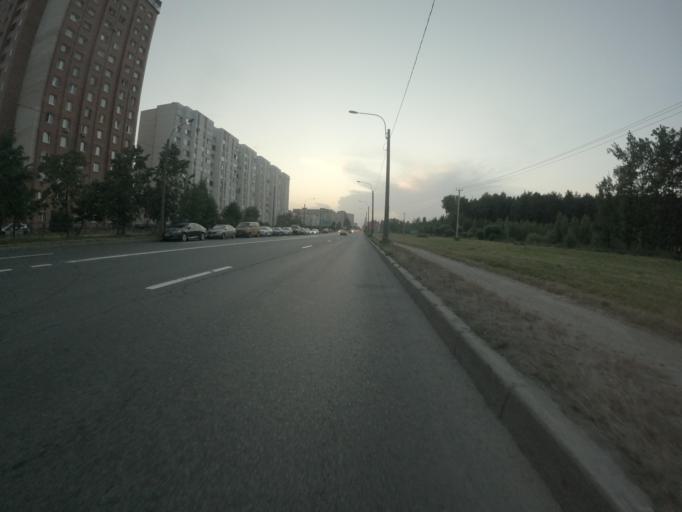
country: RU
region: St.-Petersburg
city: Krasnogvargeisky
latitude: 59.9486
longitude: 30.5028
